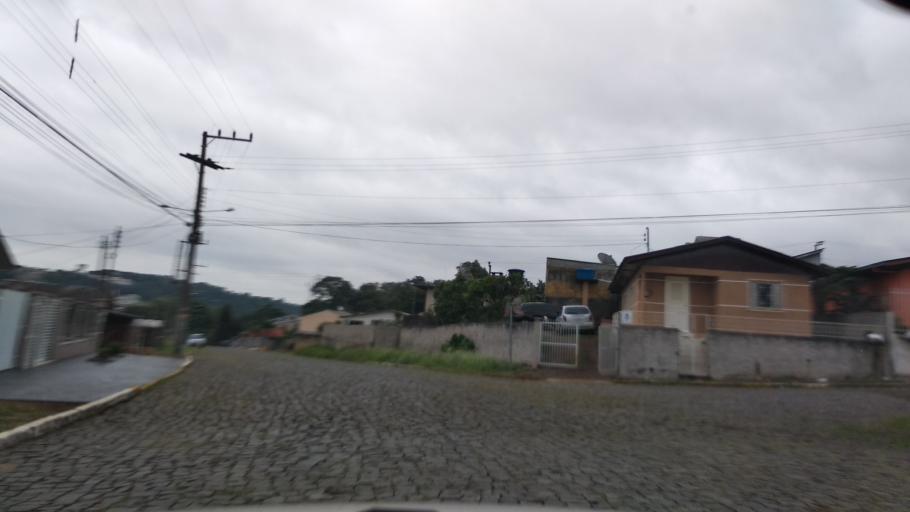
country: BR
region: Santa Catarina
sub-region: Videira
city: Videira
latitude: -26.9874
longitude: -51.1741
